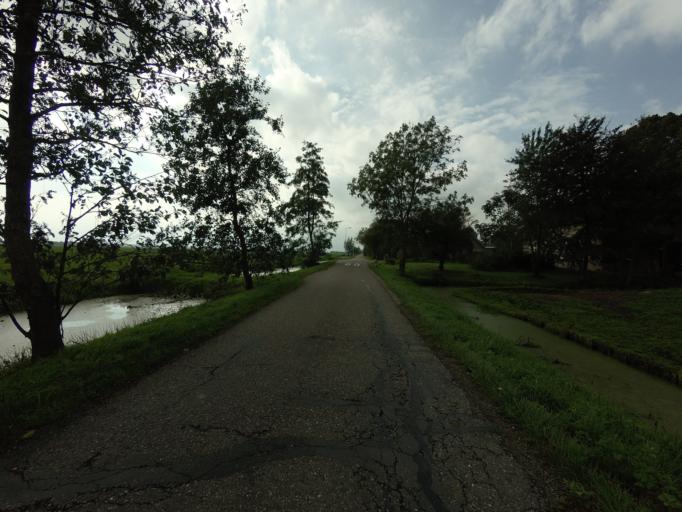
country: NL
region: South Holland
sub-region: Molenwaard
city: Liesveld
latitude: 51.8940
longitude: 4.8308
